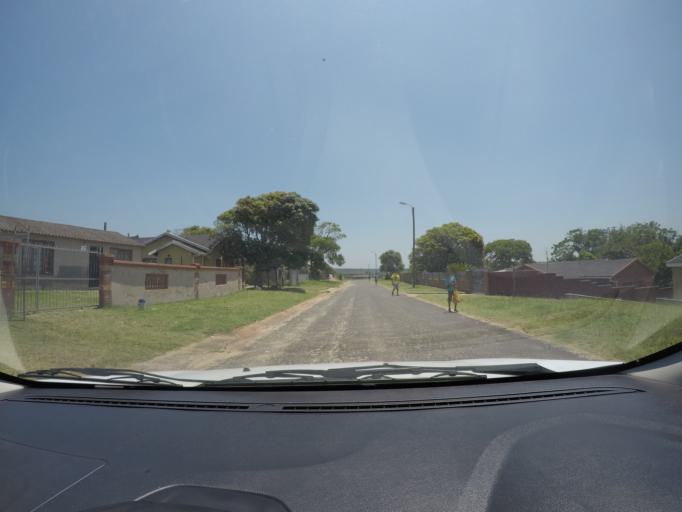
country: ZA
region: KwaZulu-Natal
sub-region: uThungulu District Municipality
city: eSikhawini
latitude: -28.8775
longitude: 31.9063
